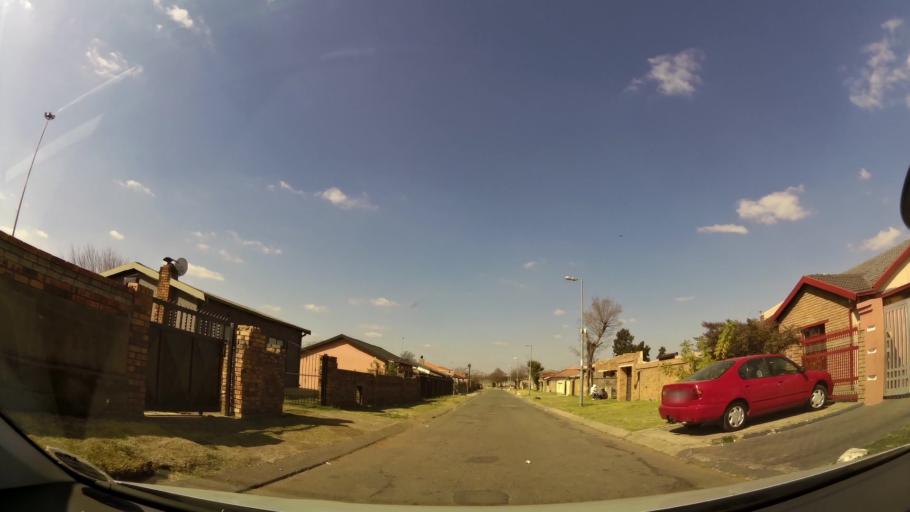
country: ZA
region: Gauteng
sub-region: City of Johannesburg Metropolitan Municipality
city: Soweto
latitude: -26.2476
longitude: 27.8865
